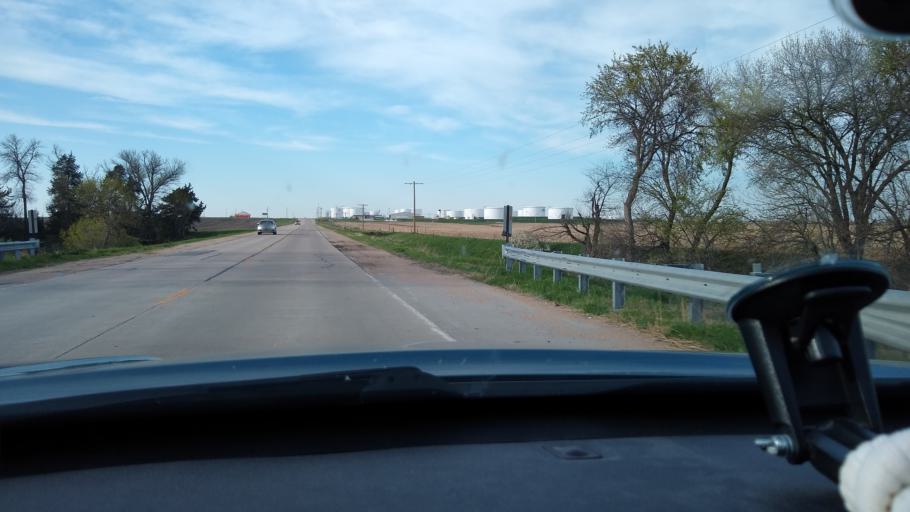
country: US
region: Nebraska
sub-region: Fillmore County
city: Geneva
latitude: 40.5438
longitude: -97.5958
